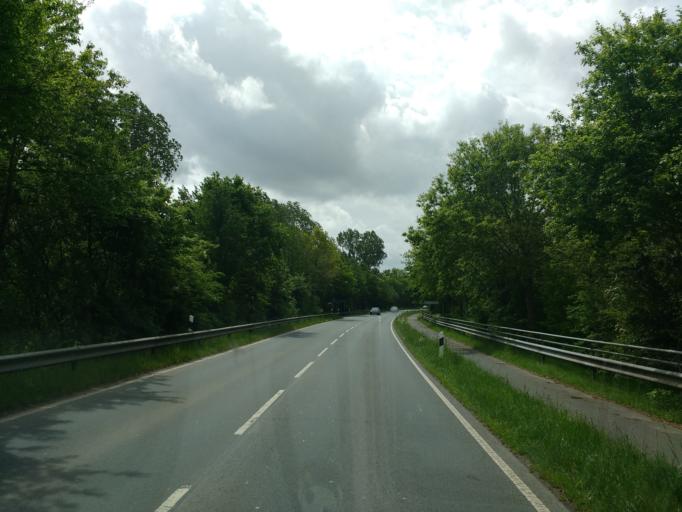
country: DE
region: Lower Saxony
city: Jever
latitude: 53.5832
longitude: 7.9103
